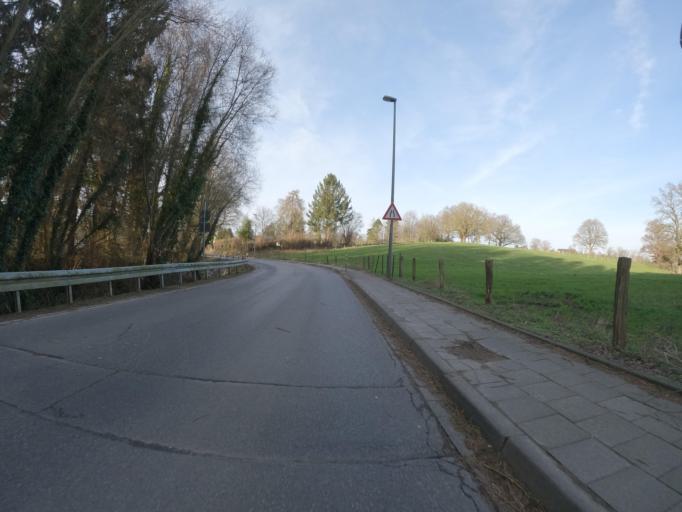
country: DE
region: North Rhine-Westphalia
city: Stolberg
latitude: 50.7370
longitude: 6.1611
